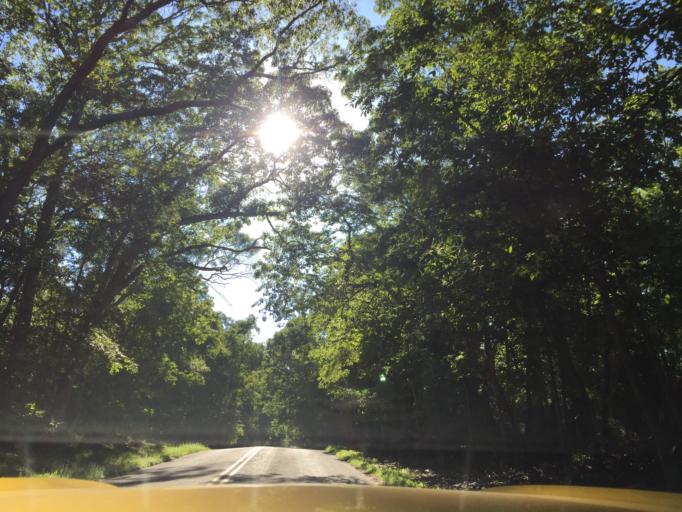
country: US
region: New York
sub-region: Suffolk County
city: Southold
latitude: 41.0423
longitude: -72.3984
